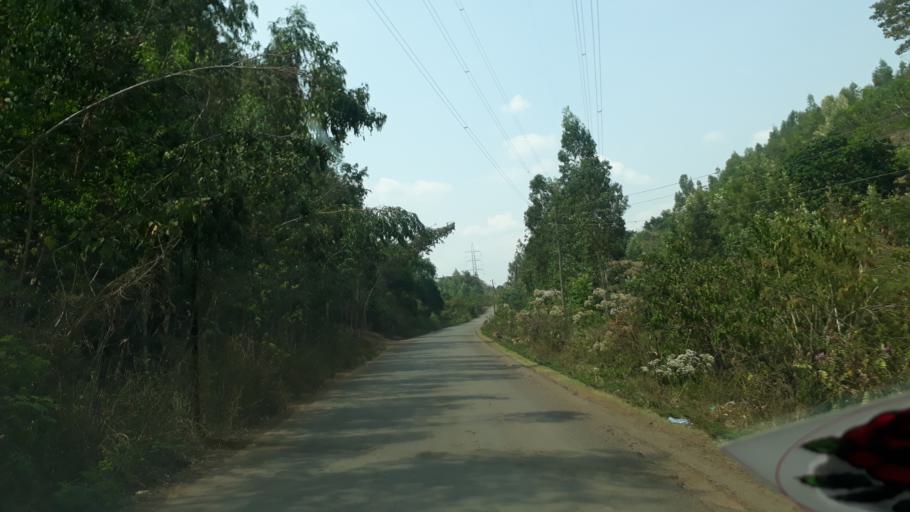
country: ET
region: Oromiya
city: Agaro
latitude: 7.9246
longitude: 36.5153
